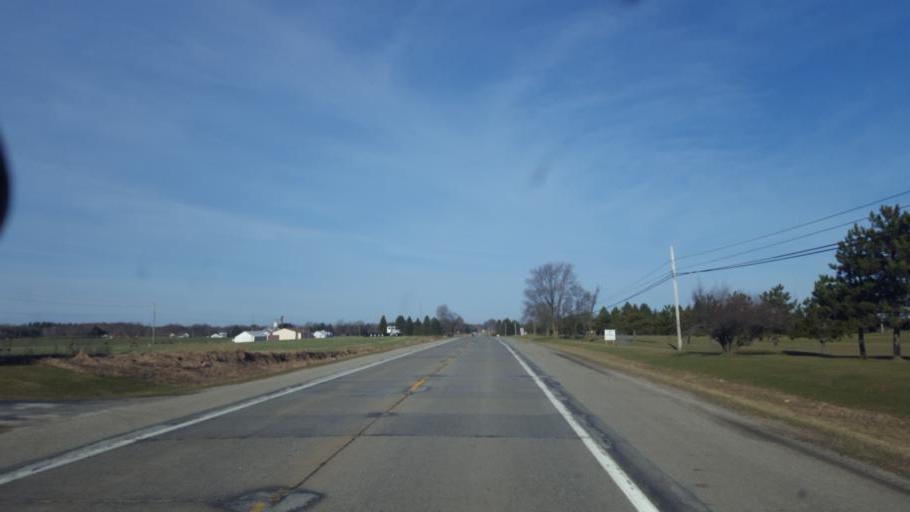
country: US
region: Michigan
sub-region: Montcalm County
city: Edmore
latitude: 43.4083
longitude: -85.0538
